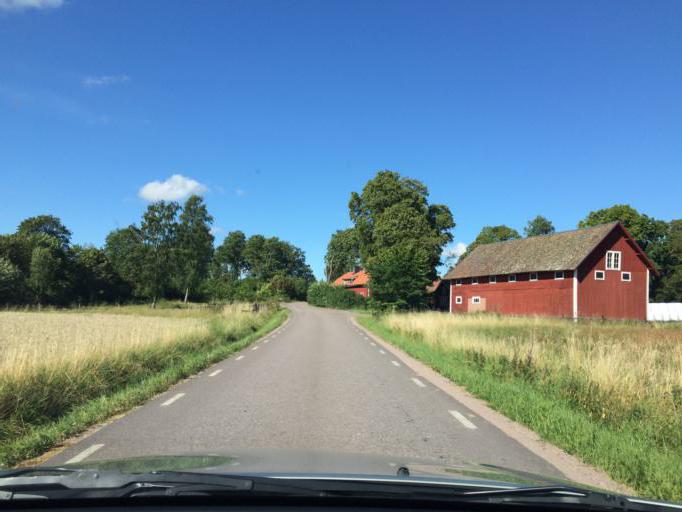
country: SE
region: Soedermanland
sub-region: Eskilstuna Kommun
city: Kvicksund
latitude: 59.5058
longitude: 16.3804
